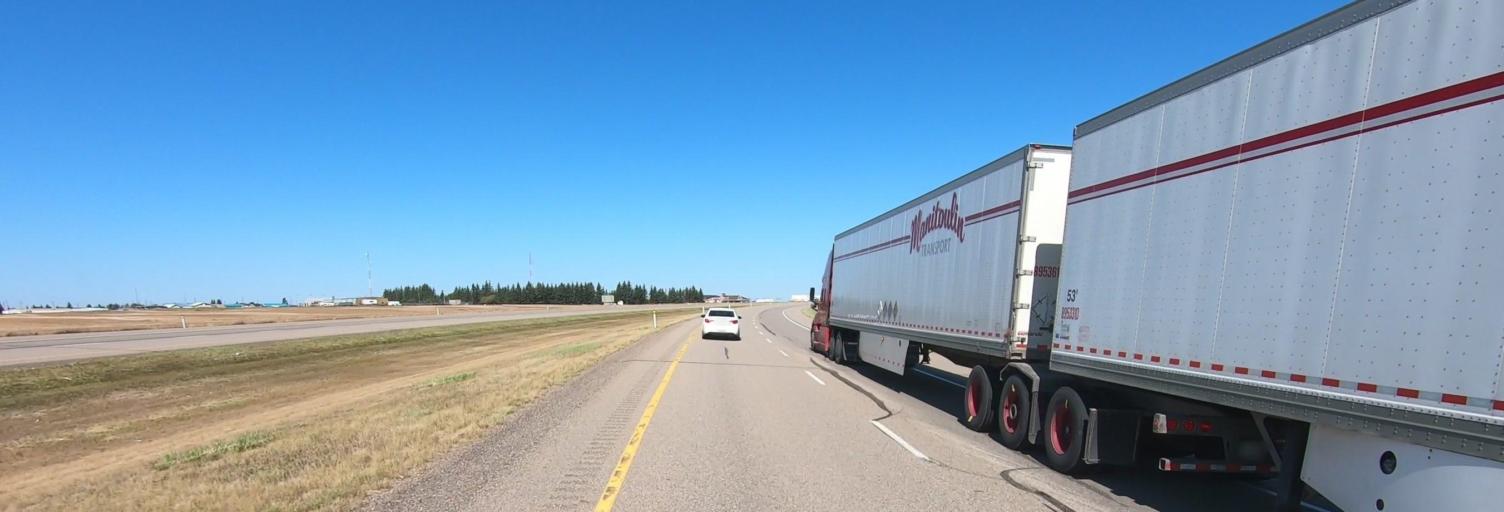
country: CA
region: Alberta
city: Bassano
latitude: 50.7863
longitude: -112.4415
